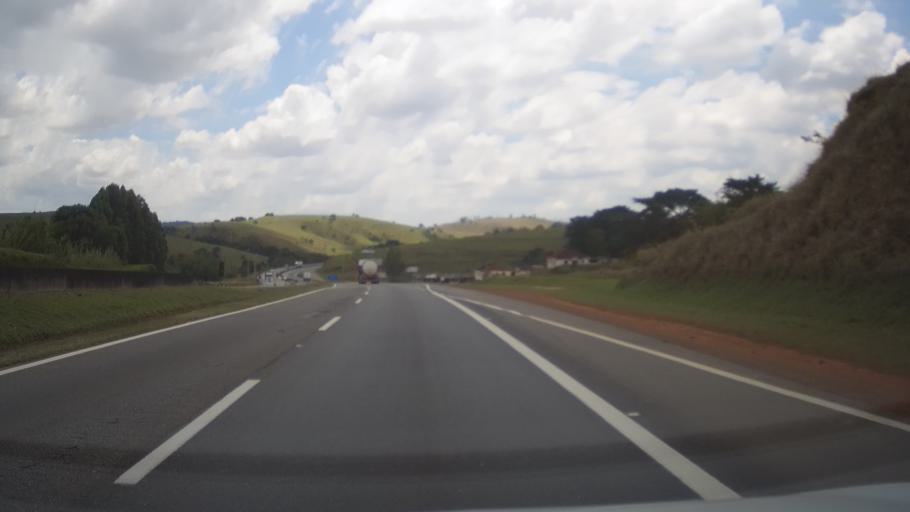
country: BR
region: Minas Gerais
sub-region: Campanha
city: Campanha
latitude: -21.7146
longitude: -45.3765
